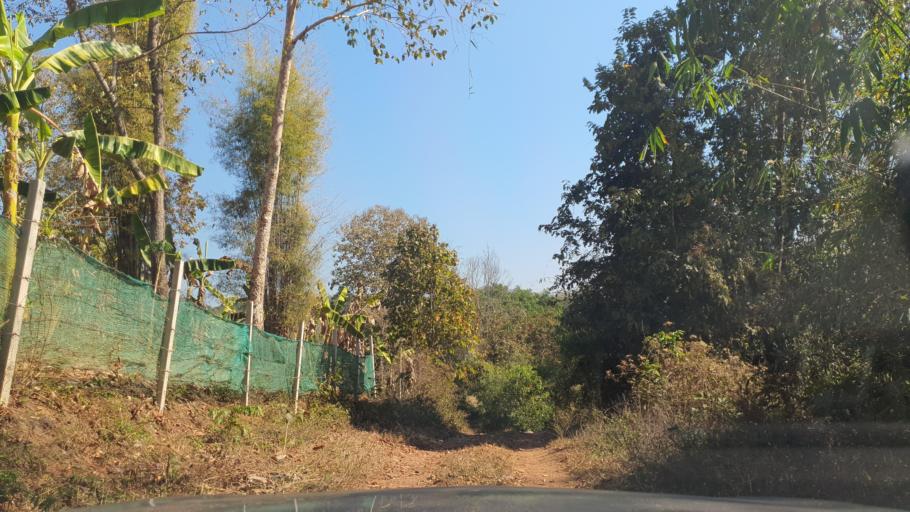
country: TH
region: Chiang Mai
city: Mae On
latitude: 18.8708
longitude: 99.2602
